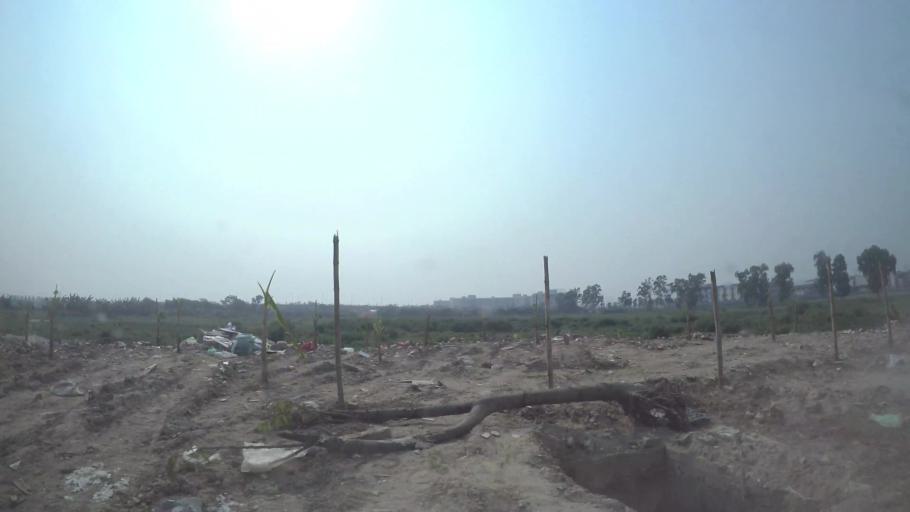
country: VN
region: Ha Noi
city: Ha Dong
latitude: 20.9442
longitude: 105.7891
